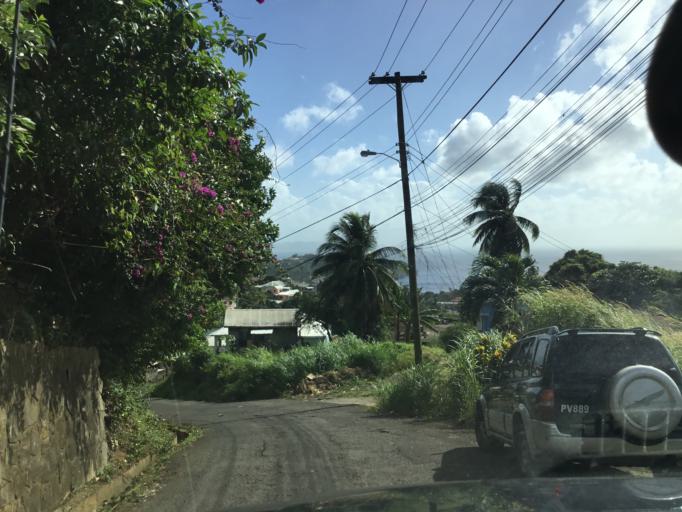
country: VC
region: Saint George
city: Kingstown
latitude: 13.1679
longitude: -61.2192
